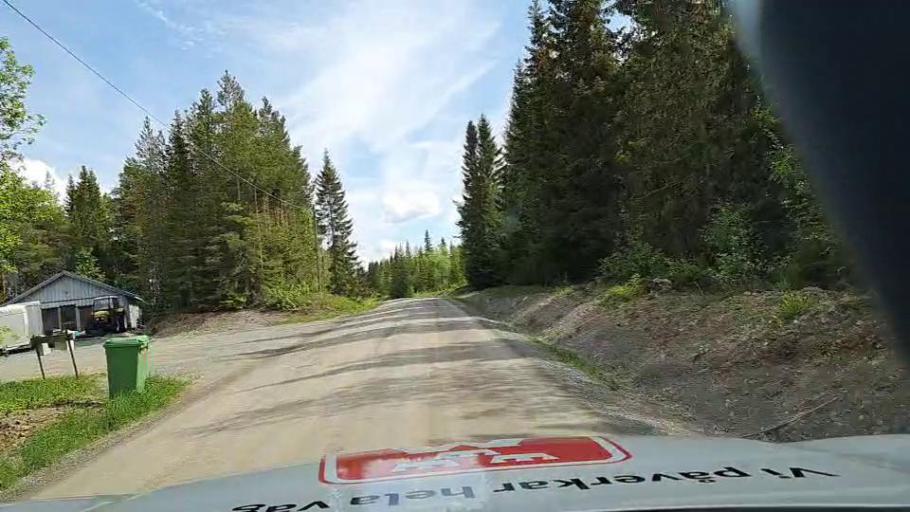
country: SE
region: Jaemtland
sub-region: OEstersunds Kommun
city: Brunflo
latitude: 63.0081
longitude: 14.7884
